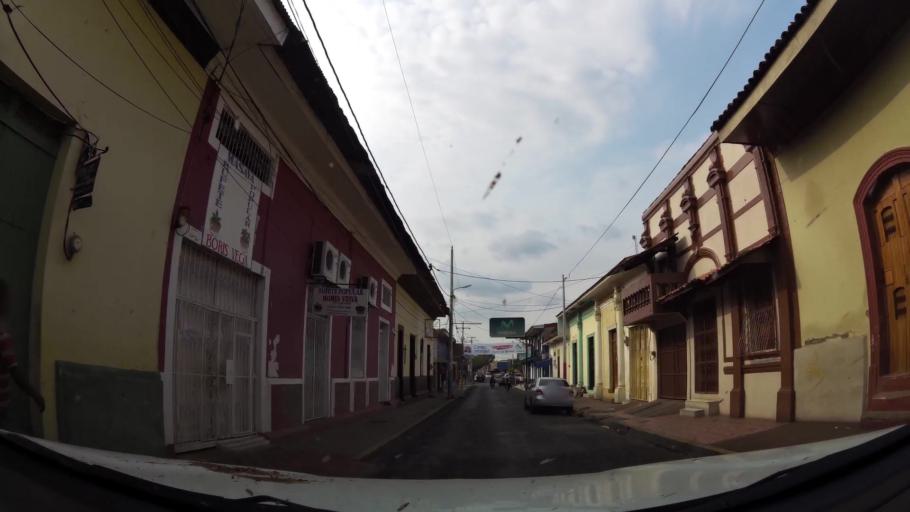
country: NI
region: Masaya
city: Masaya
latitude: 11.9727
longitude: -86.0941
